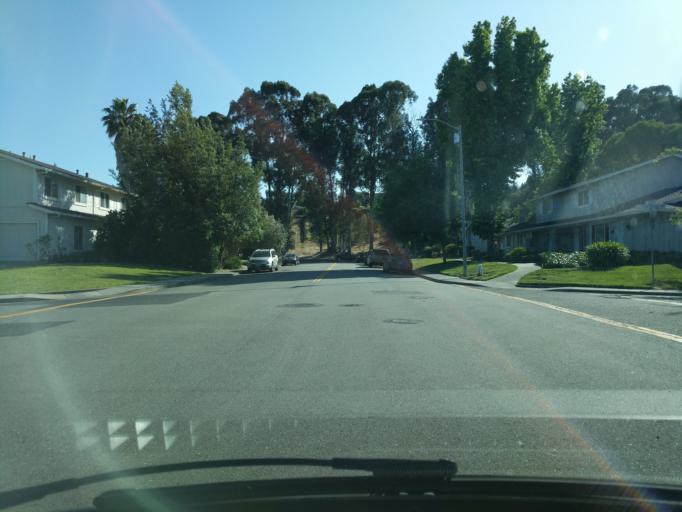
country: US
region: California
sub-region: Contra Costa County
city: San Ramon
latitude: 37.7685
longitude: -121.9880
